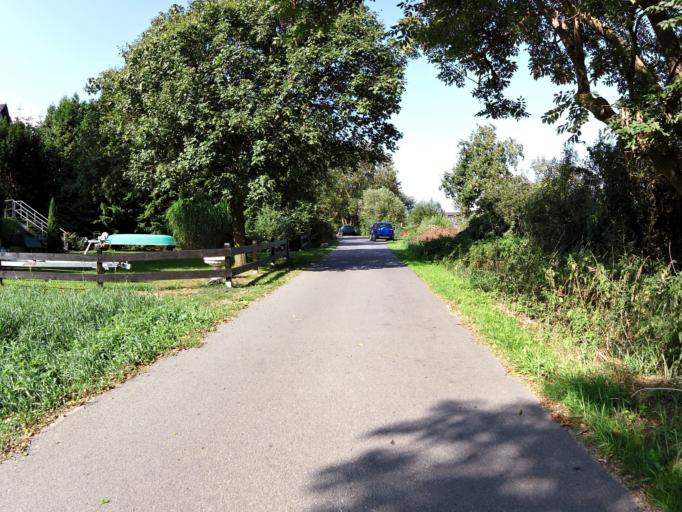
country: DE
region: Mecklenburg-Vorpommern
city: Seebad Bansin
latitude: 53.9714
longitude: 14.0664
